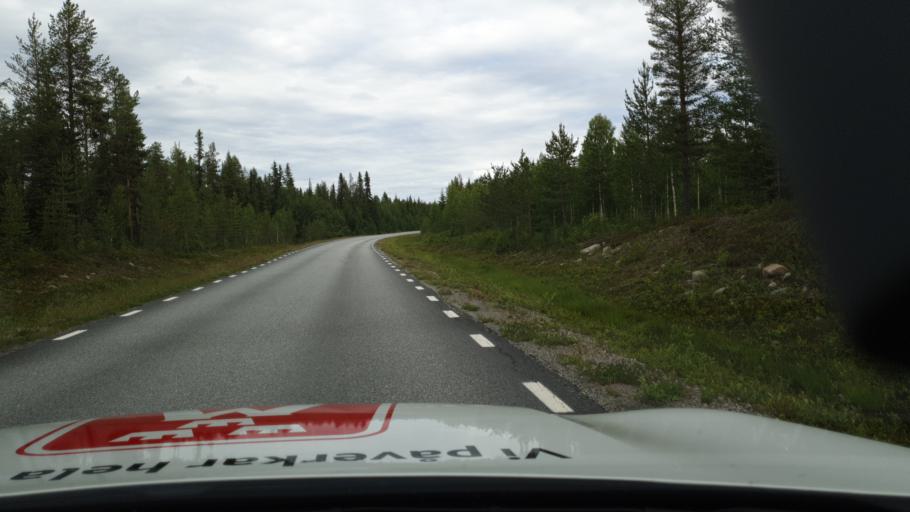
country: SE
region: Vaesterbotten
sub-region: Sorsele Kommun
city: Sorsele
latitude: 65.5256
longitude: 17.3903
